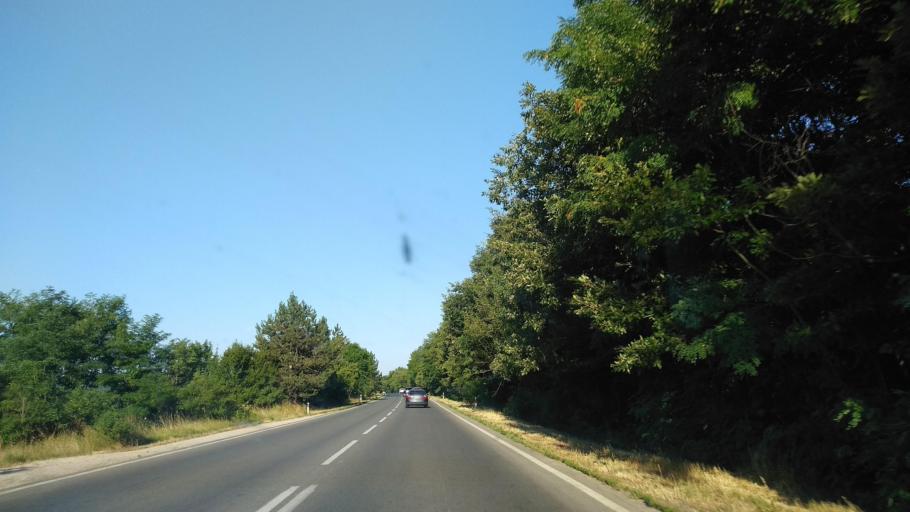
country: BG
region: Gabrovo
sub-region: Obshtina Sevlievo
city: Sevlievo
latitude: 43.0475
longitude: 25.2387
